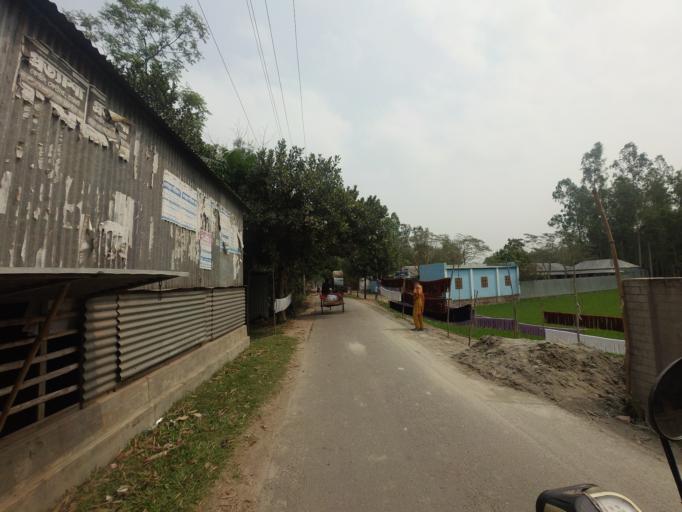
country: BD
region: Rajshahi
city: Sirajganj
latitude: 24.3346
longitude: 89.6833
